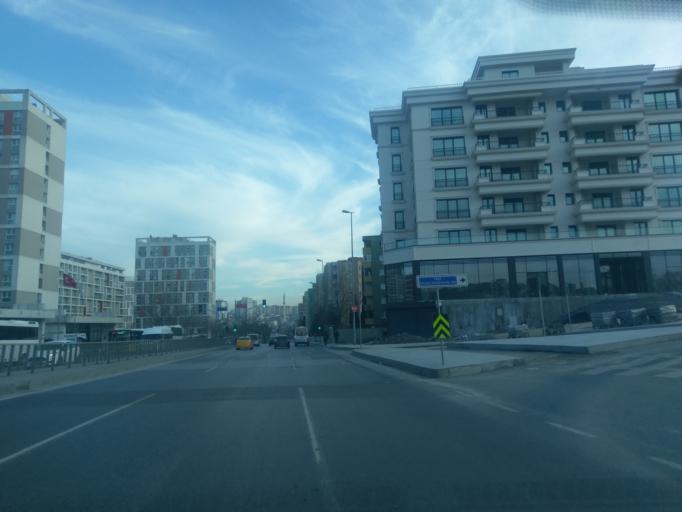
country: TR
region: Istanbul
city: Mahmutbey
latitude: 41.0393
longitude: 28.7613
